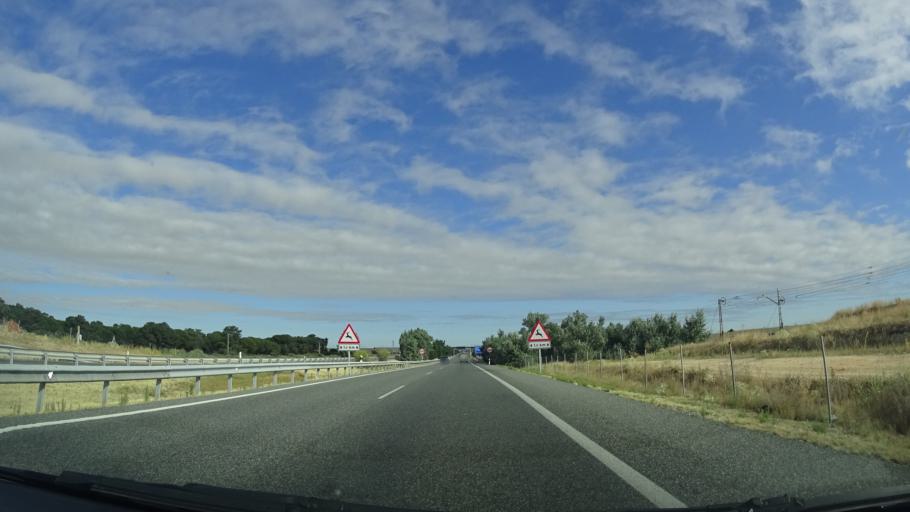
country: ES
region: Castille and Leon
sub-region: Provincia de Valladolid
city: Medina del Campo
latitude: 41.2803
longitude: -4.8922
